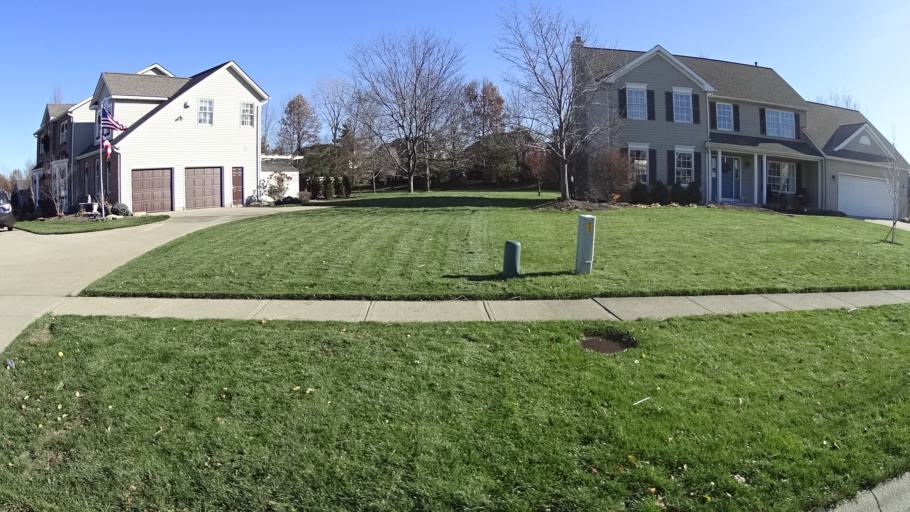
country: US
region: Ohio
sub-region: Lorain County
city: Avon Center
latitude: 41.4264
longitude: -81.9975
